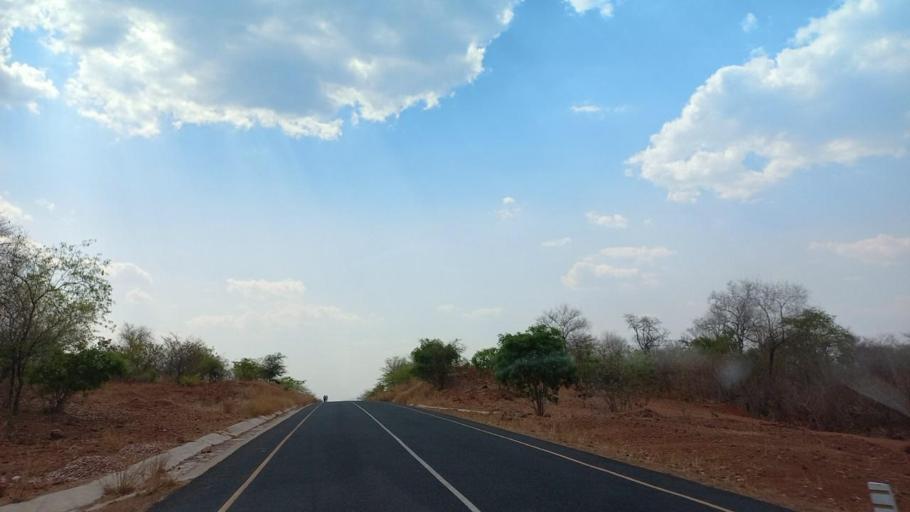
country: ZM
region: Lusaka
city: Luangwa
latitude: -15.2169
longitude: 30.2349
